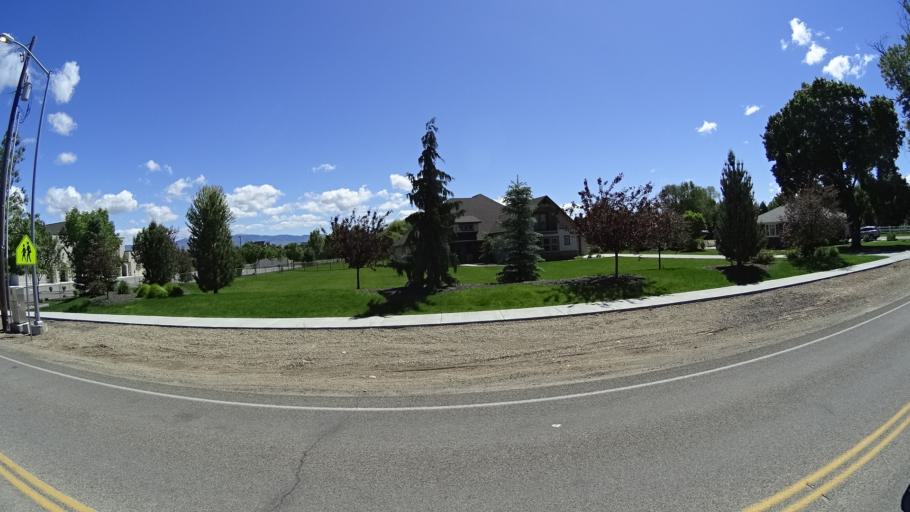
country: US
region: Idaho
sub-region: Ada County
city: Eagle
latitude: 43.6592
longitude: -116.3745
